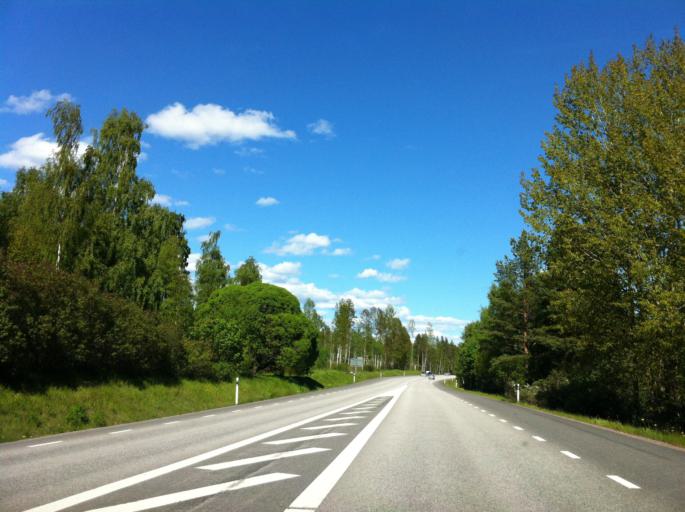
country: SE
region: Dalarna
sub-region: Rattviks Kommun
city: Vikarbyn
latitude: 60.9091
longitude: 15.0068
